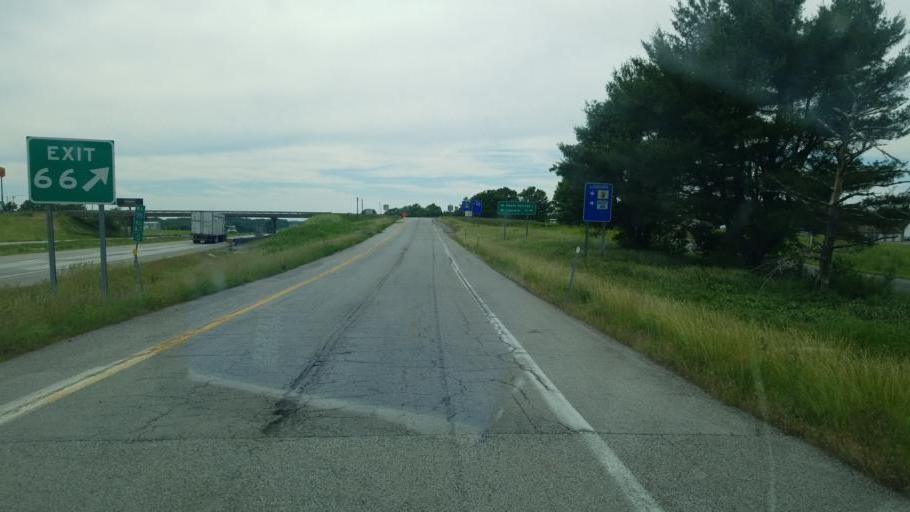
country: US
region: Missouri
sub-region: Saline County
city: Sweet Springs
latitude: 38.9772
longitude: -93.4128
